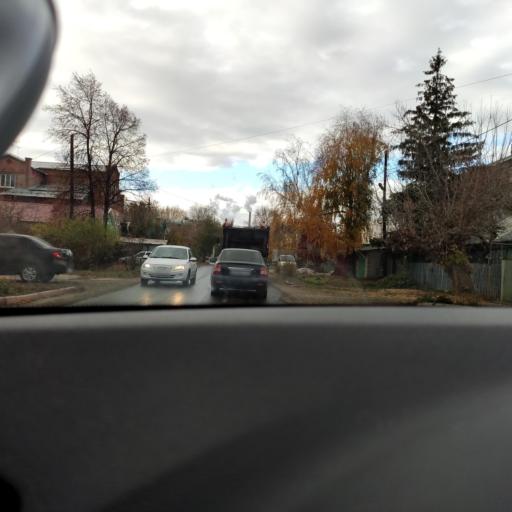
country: RU
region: Samara
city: Petra-Dubrava
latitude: 53.2489
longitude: 50.3161
